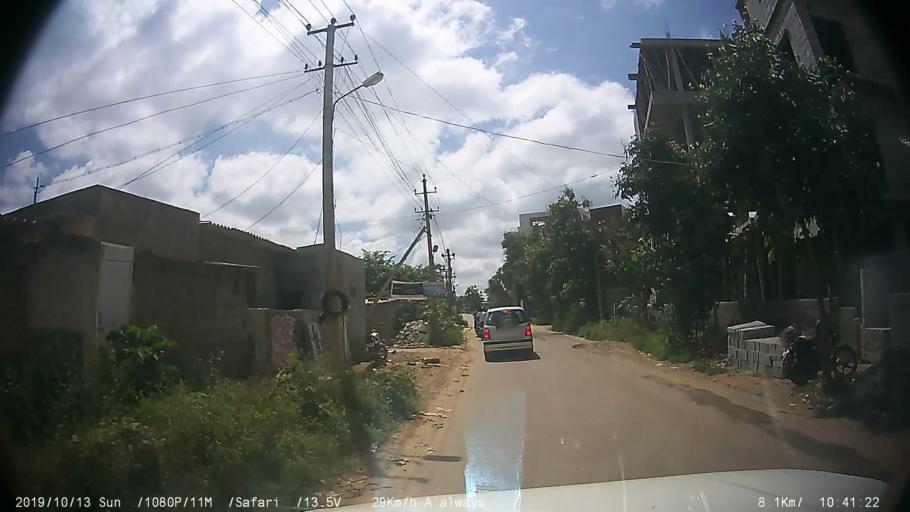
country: IN
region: Karnataka
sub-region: Bangalore Urban
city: Anekal
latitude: 12.8265
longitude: 77.6496
